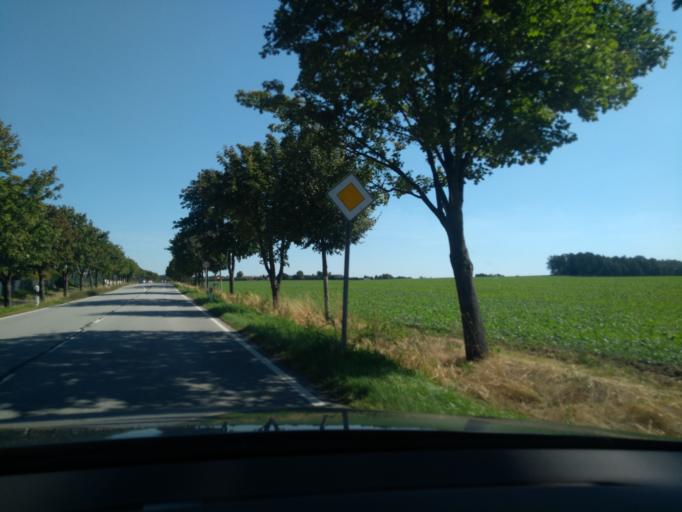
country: DE
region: Saxony
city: Goda
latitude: 51.1929
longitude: 14.3418
